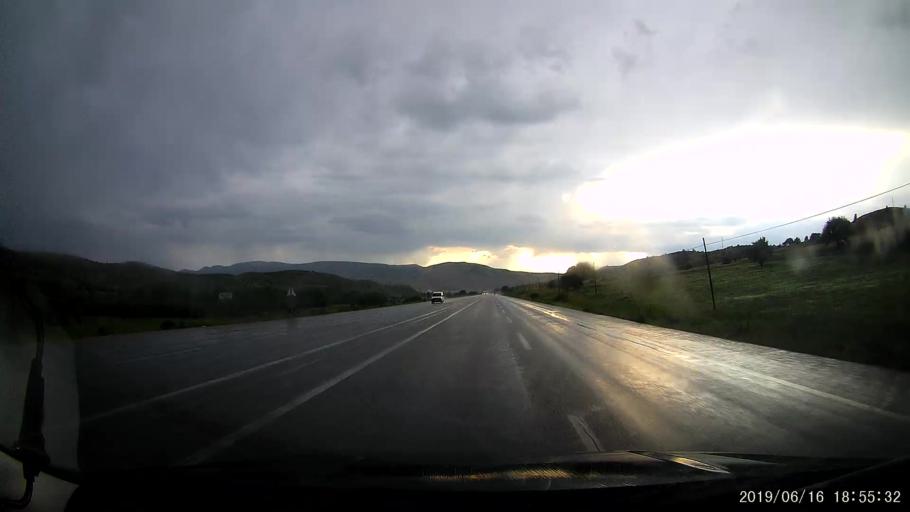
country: TR
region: Erzincan
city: Refahiye
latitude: 39.9005
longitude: 38.8254
